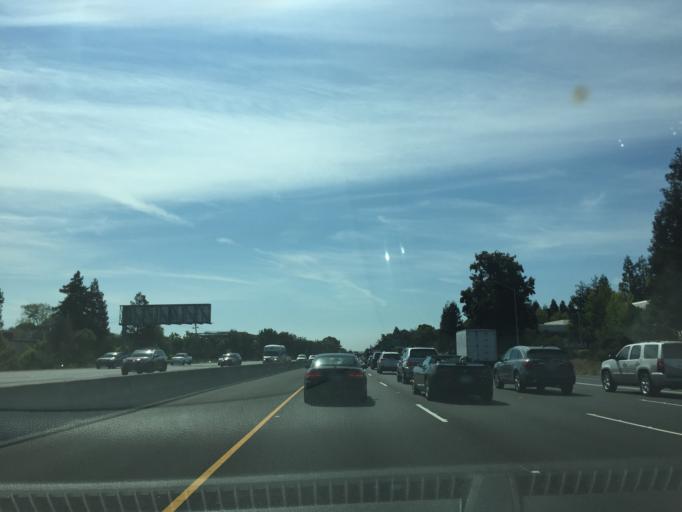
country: US
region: California
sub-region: San Mateo County
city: North Fair Oaks
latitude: 37.4820
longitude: -122.1779
